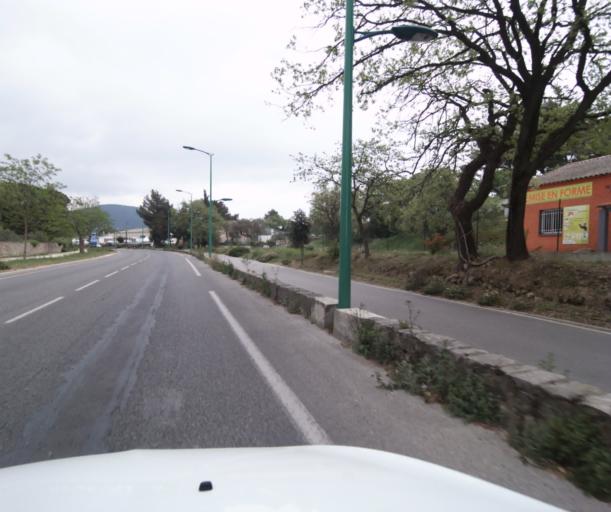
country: FR
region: Provence-Alpes-Cote d'Azur
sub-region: Departement du Var
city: Le Pradet
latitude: 43.1089
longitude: 6.0406
